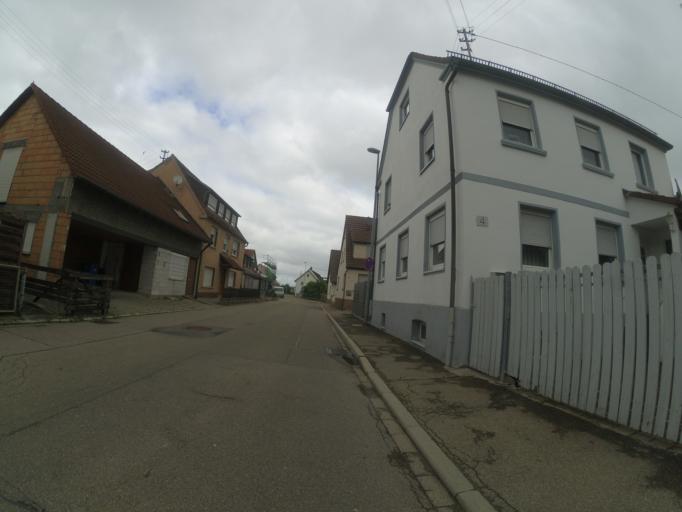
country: DE
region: Baden-Wuerttemberg
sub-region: Tuebingen Region
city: Bernstadt
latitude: 48.4997
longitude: 10.0267
